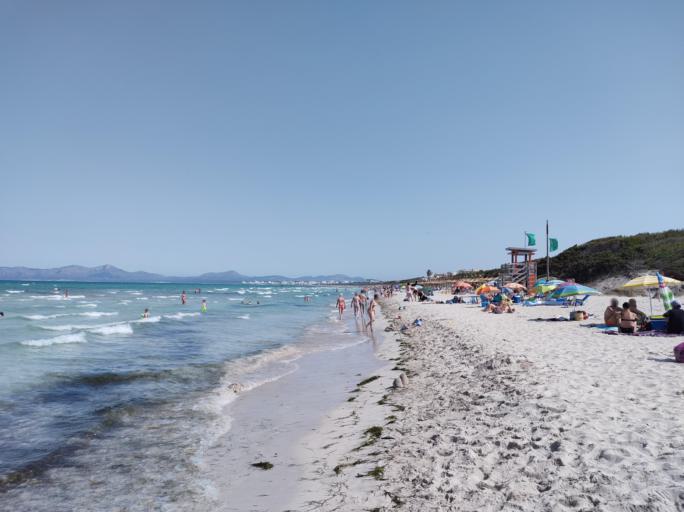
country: ES
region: Balearic Islands
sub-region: Illes Balears
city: Port d'Alcudia
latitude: 39.7936
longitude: 3.1258
